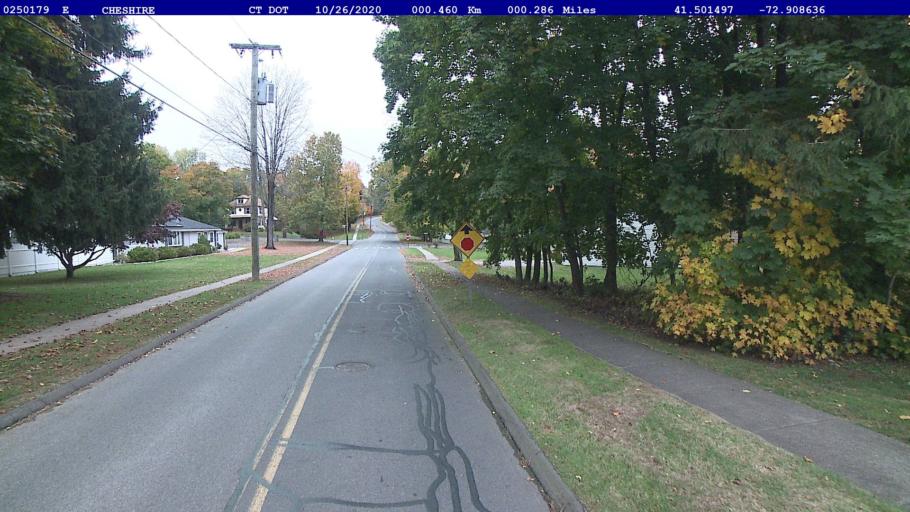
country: US
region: Connecticut
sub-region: New Haven County
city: Cheshire
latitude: 41.5015
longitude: -72.9086
